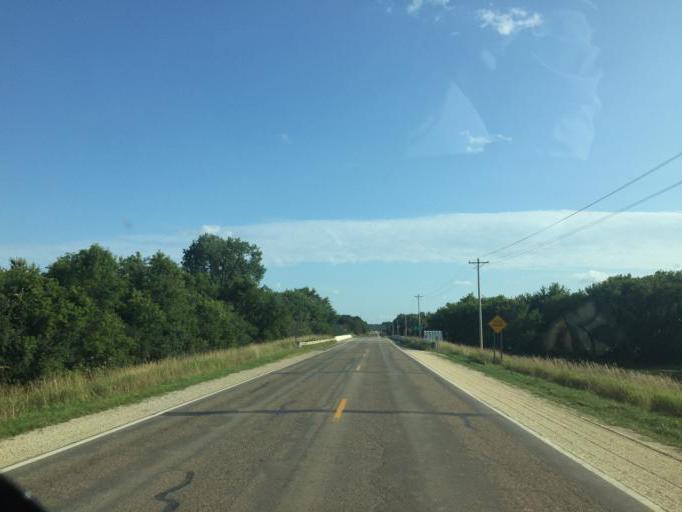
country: US
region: Minnesota
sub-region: Olmsted County
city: Rochester
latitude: 43.9804
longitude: -92.5582
